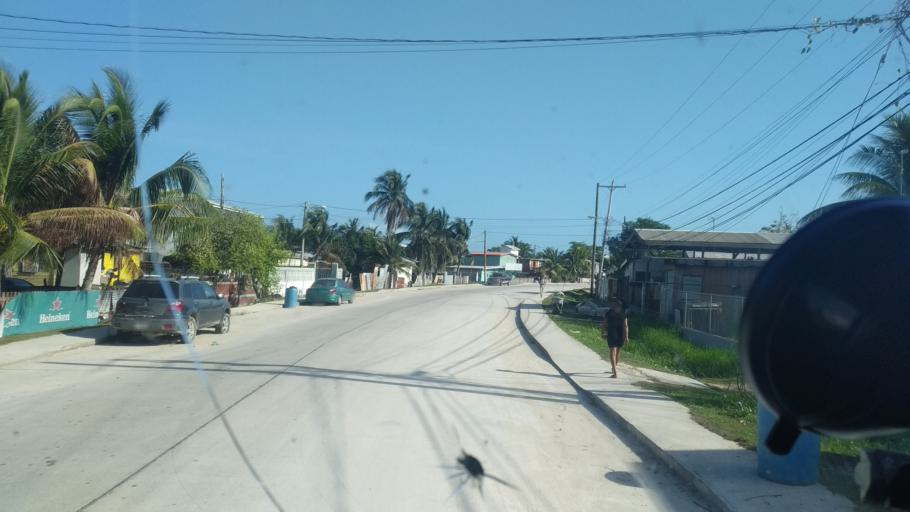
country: BZ
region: Belize
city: Belize City
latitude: 17.4858
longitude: -88.2020
